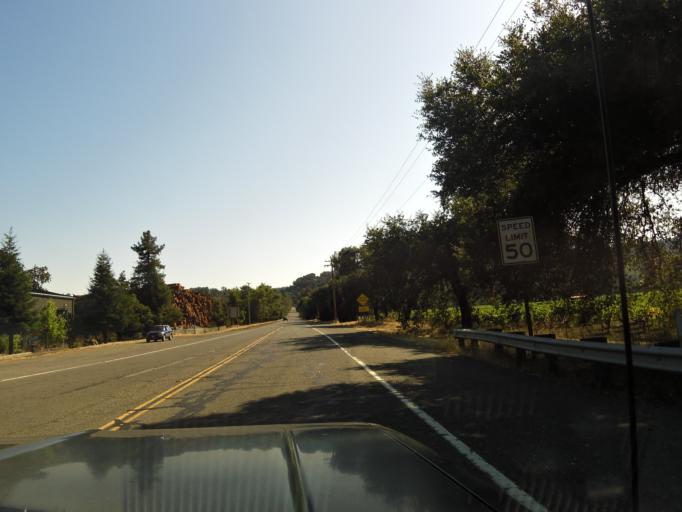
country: US
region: California
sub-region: Sonoma County
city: Cloverdale
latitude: 38.8256
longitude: -123.0165
